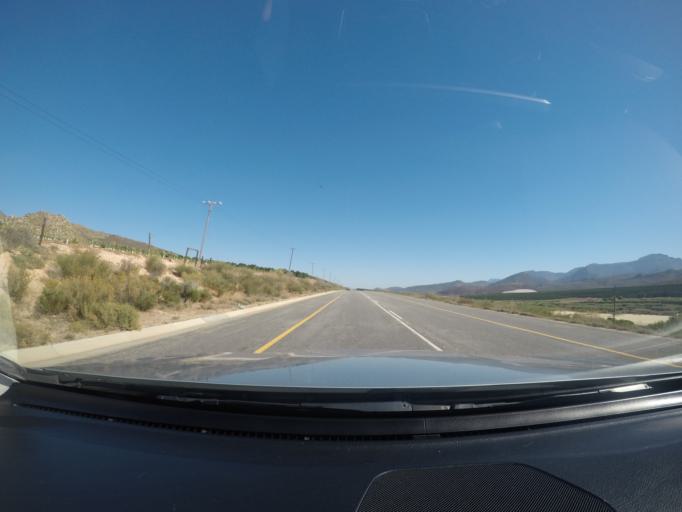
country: ZA
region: Western Cape
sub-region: West Coast District Municipality
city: Clanwilliam
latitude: -32.4906
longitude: 18.9650
